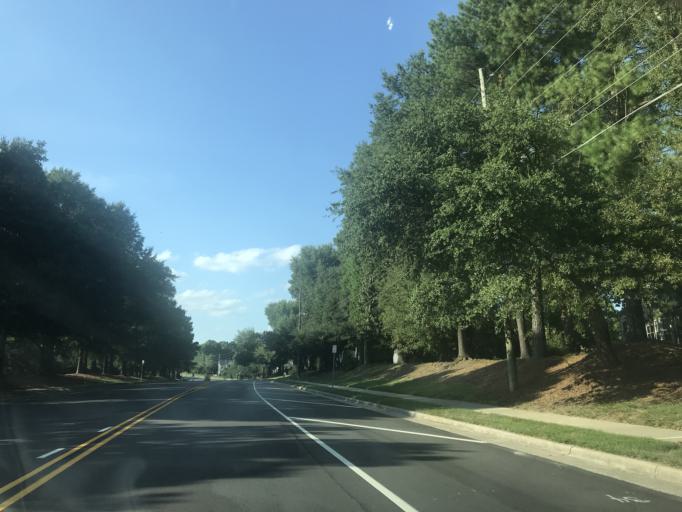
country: US
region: North Carolina
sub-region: Wake County
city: Knightdale
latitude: 35.7813
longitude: -78.5451
